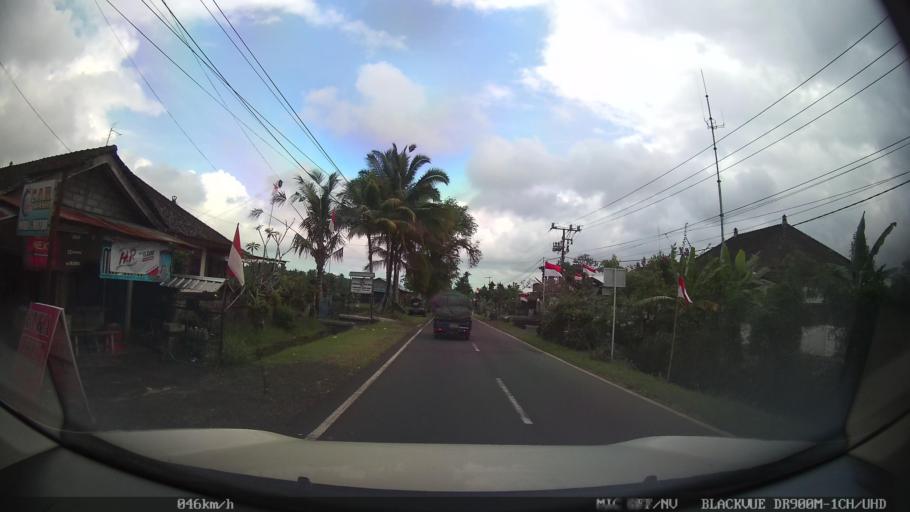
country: ID
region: Bali
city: Pohgending Kawan
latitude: -8.4389
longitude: 115.1422
